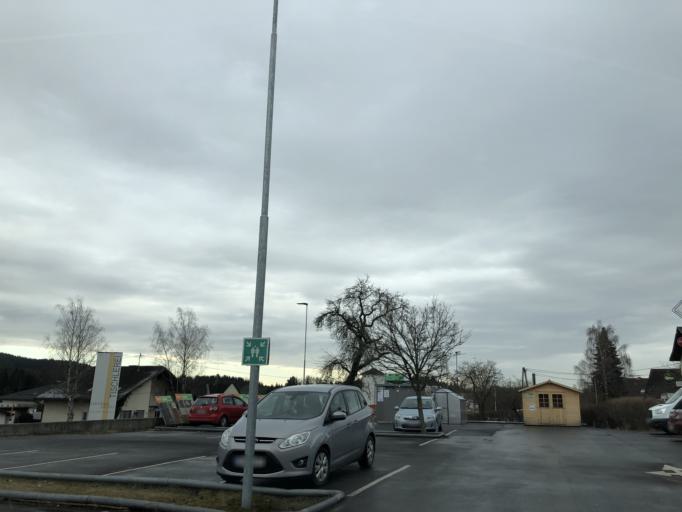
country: AT
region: Upper Austria
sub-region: Politischer Bezirk Freistadt
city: Freistadt
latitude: 48.4947
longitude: 14.5022
